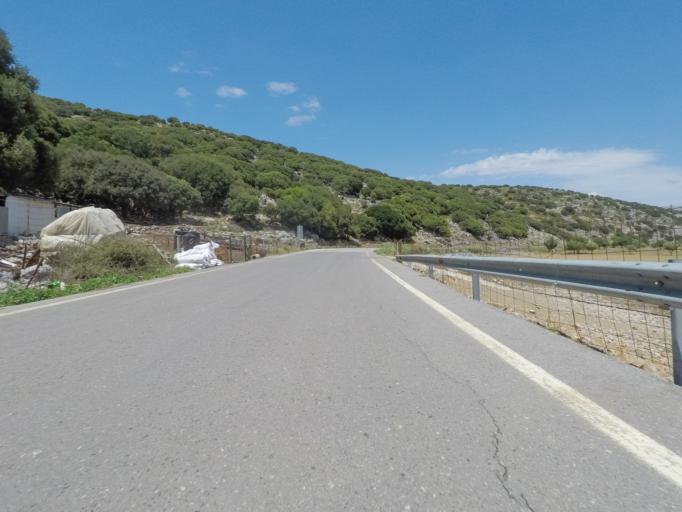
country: GR
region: Crete
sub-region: Nomos Irakleiou
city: Mokhos
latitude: 35.1952
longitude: 25.4482
